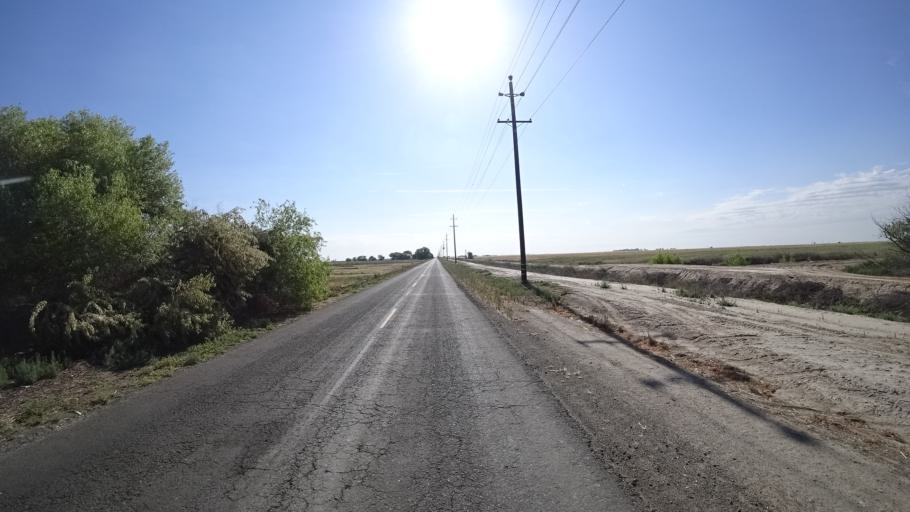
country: US
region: California
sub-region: Kings County
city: Lemoore
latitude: 36.2256
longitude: -119.7388
